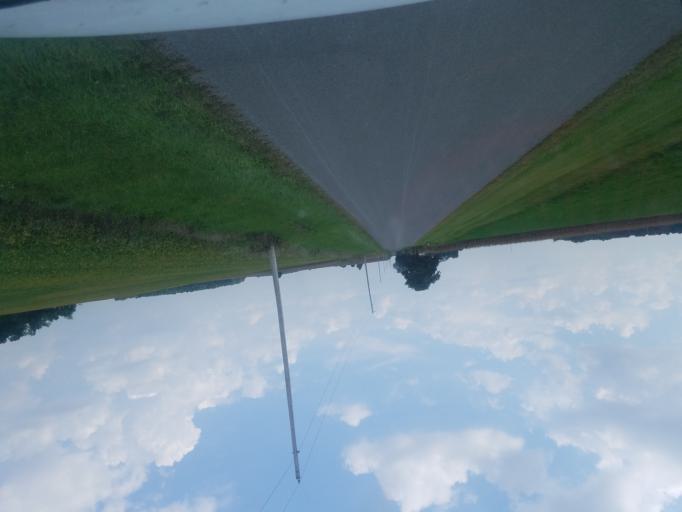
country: US
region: Ohio
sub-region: Hardin County
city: Ada
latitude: 40.6377
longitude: -83.8621
